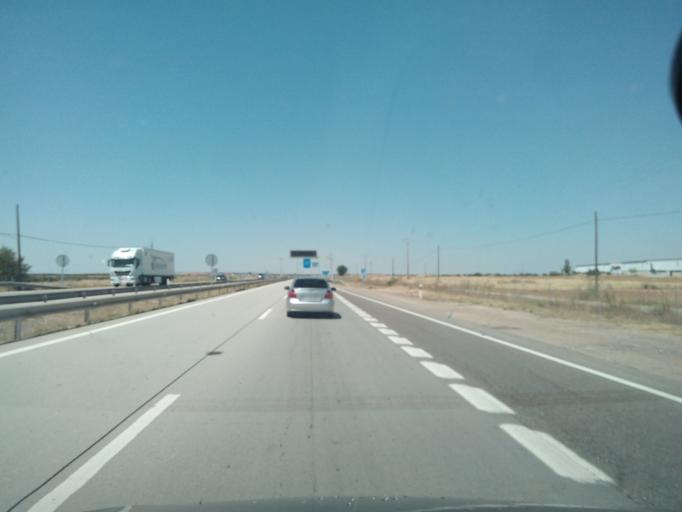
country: ES
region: Castille-La Mancha
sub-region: Province of Toledo
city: Dosbarrios
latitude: 39.8934
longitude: -3.4727
